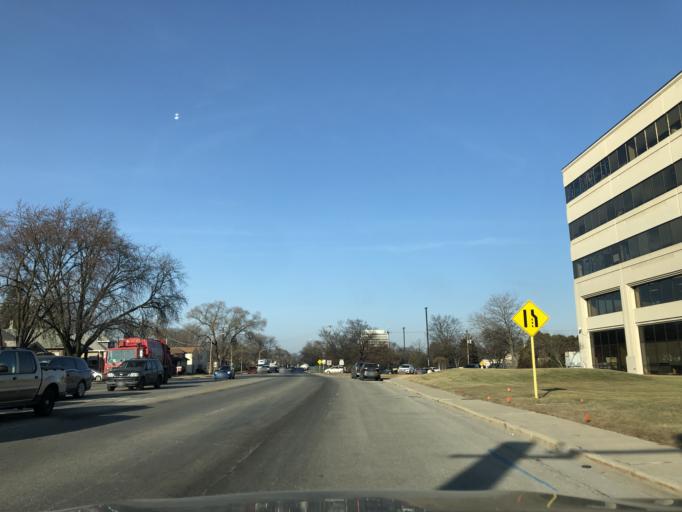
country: US
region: Illinois
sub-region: Cook County
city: Maywood
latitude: 41.8647
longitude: -87.8332
